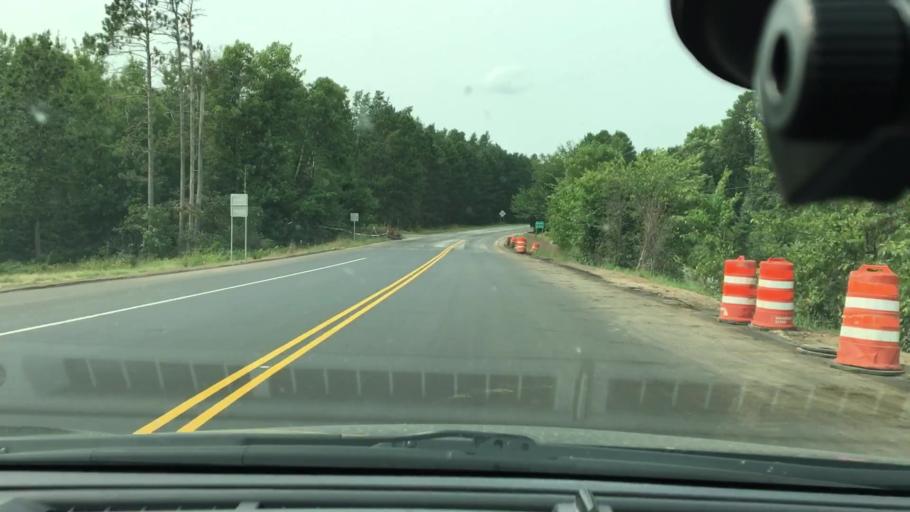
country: US
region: Minnesota
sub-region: Crow Wing County
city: Cross Lake
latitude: 46.7359
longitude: -93.9601
